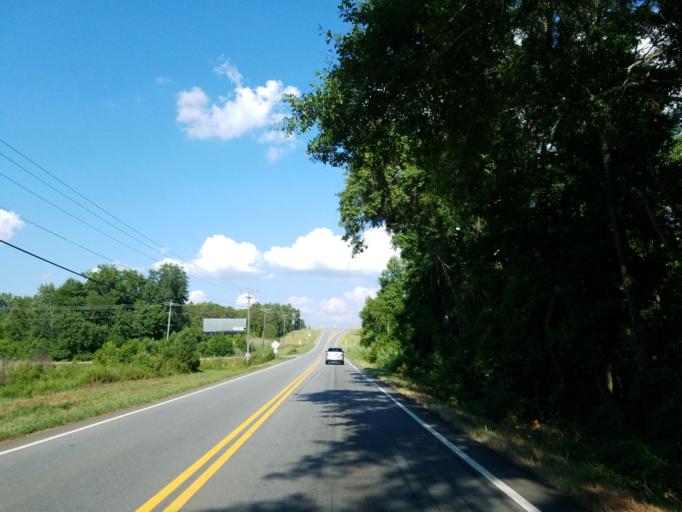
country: US
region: Georgia
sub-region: Houston County
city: Perry
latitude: 32.5464
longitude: -83.7546
